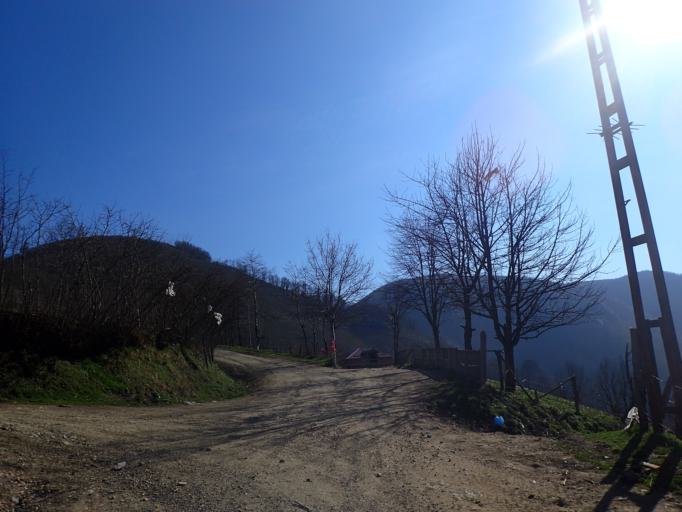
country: TR
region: Ordu
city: Camas
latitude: 40.8658
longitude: 37.4995
